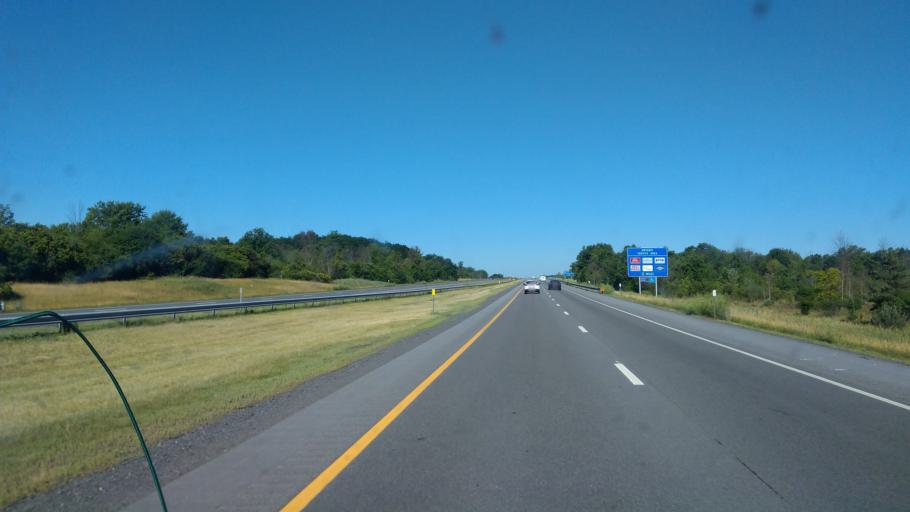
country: US
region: New York
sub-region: Livingston County
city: Caledonia
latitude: 43.0300
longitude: -77.8654
